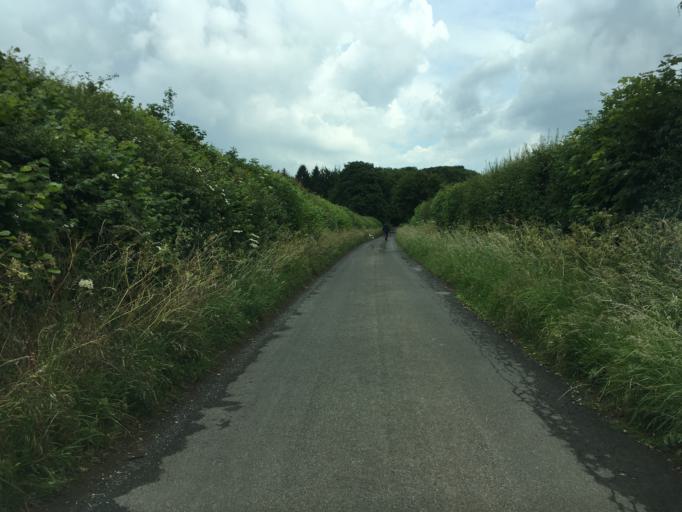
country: GB
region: England
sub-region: Gloucestershire
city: Shurdington
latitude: 51.8059
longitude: -2.0849
